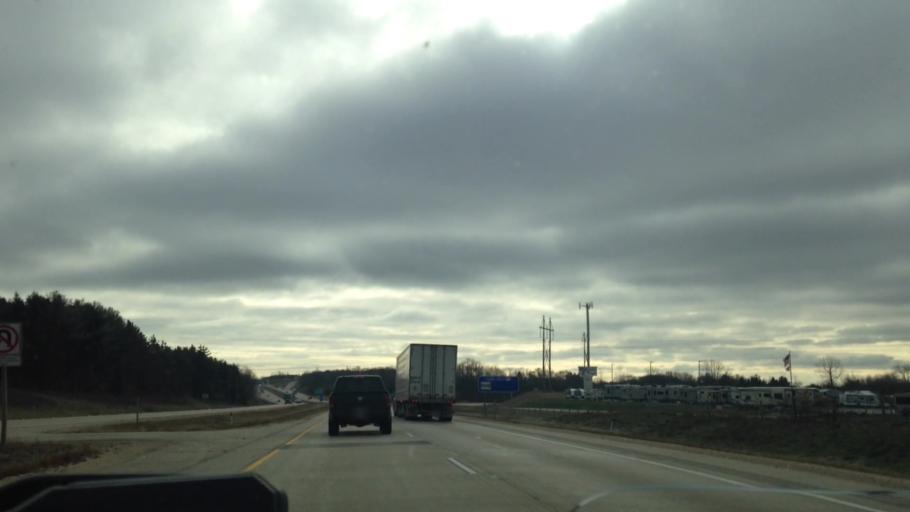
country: US
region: Wisconsin
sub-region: Washington County
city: Slinger
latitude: 43.3602
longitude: -88.2921
